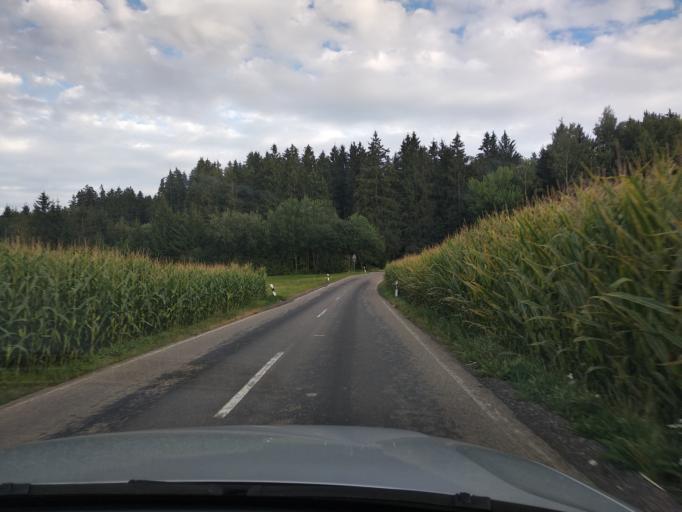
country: DE
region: Bavaria
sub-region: Swabia
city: Kronburg
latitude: 47.9313
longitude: 10.1541
